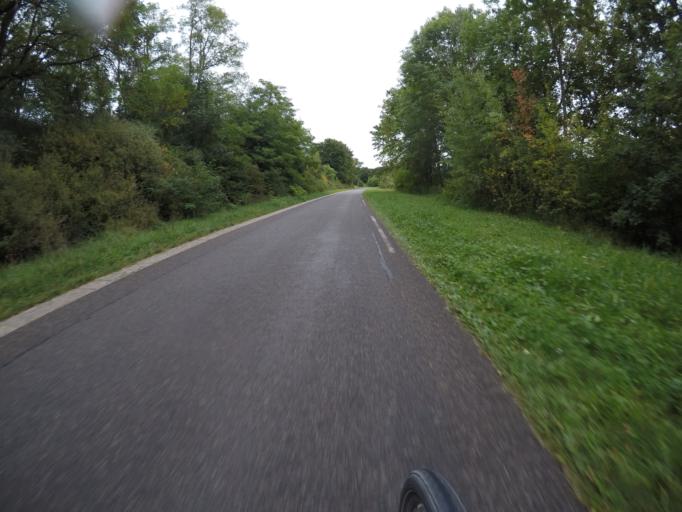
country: DE
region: Baden-Wuerttemberg
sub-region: Regierungsbezirk Stuttgart
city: Leonberg
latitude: 48.7809
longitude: 9.0257
